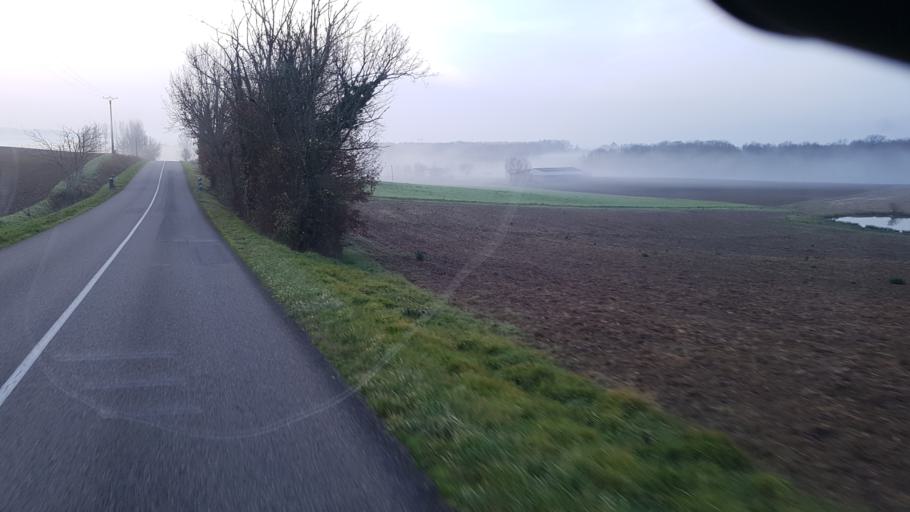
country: FR
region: Midi-Pyrenees
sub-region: Departement du Tarn-et-Garonne
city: Monteils
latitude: 44.1282
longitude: 1.5825
